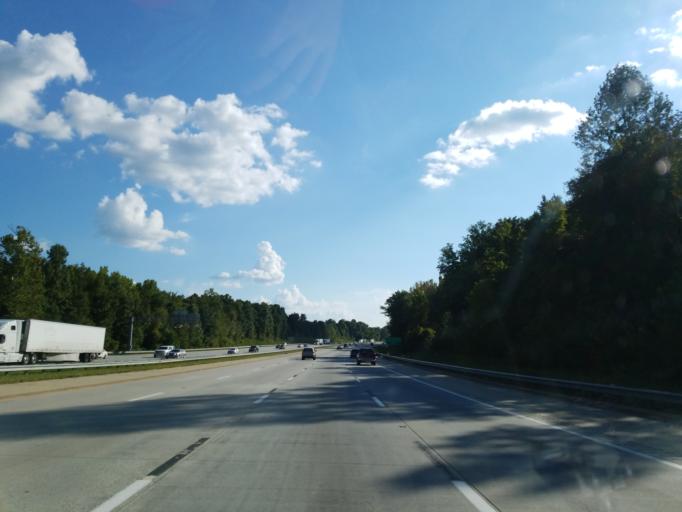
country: US
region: North Carolina
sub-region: Rowan County
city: East Spencer
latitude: 35.6874
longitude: -80.4045
